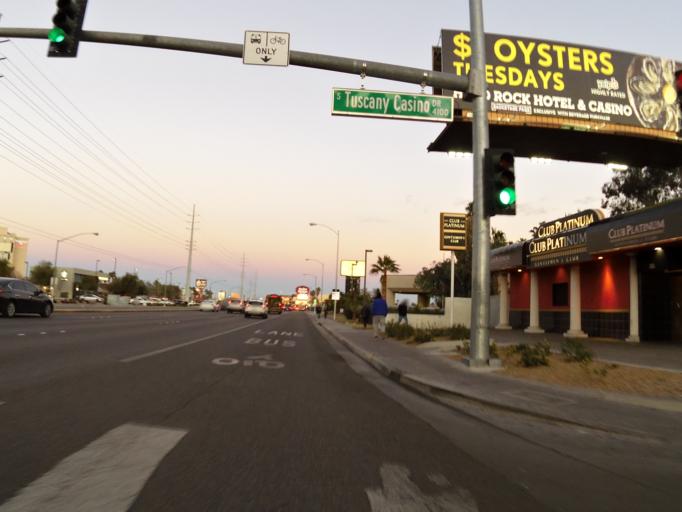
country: US
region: Nevada
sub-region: Clark County
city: Paradise
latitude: 36.1143
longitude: -115.1590
